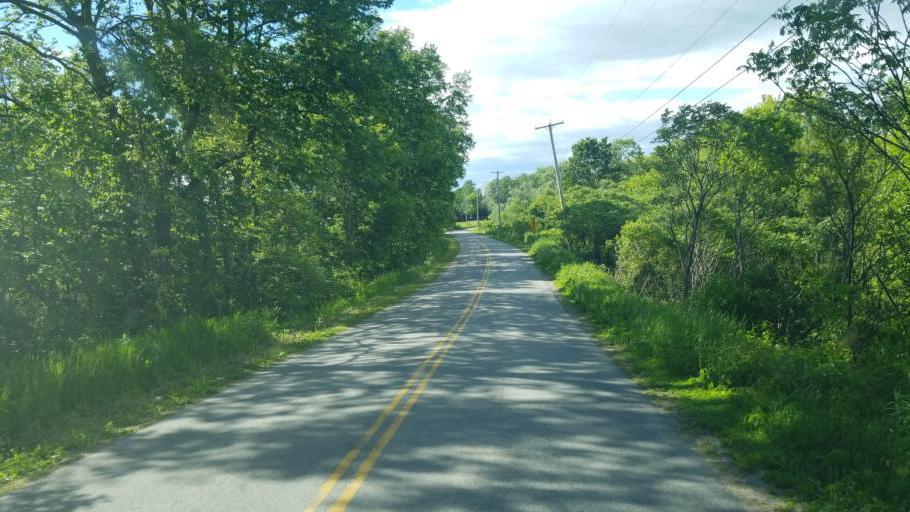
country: US
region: New York
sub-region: Montgomery County
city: Saint Johnsville
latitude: 42.9760
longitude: -74.6554
